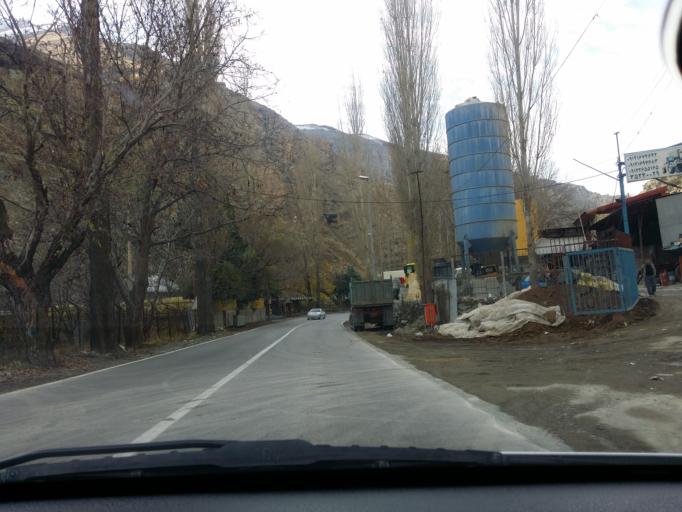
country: IR
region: Alborz
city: Karaj
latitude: 36.0169
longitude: 51.1473
